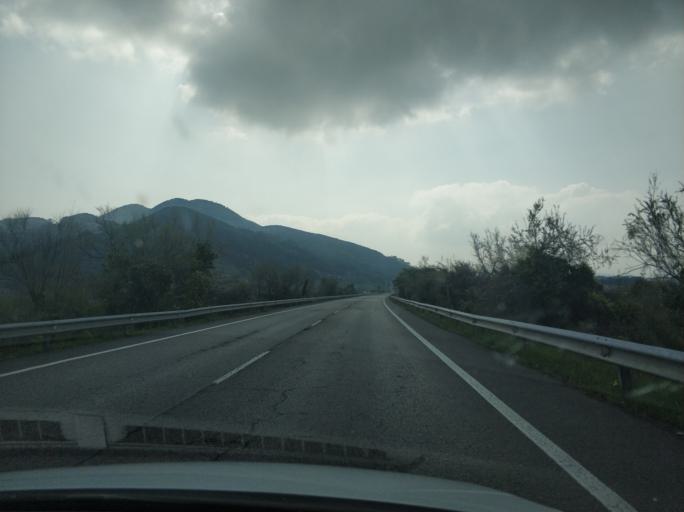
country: ES
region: Cantabria
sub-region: Provincia de Cantabria
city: Santona
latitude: 43.4567
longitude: -3.4634
